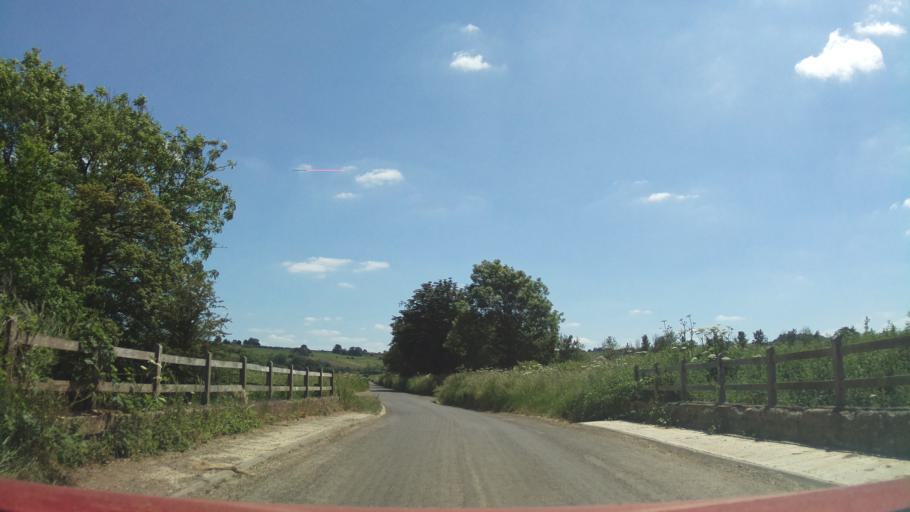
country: GB
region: England
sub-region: Wiltshire
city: Bremhill
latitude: 51.4827
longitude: -2.0400
